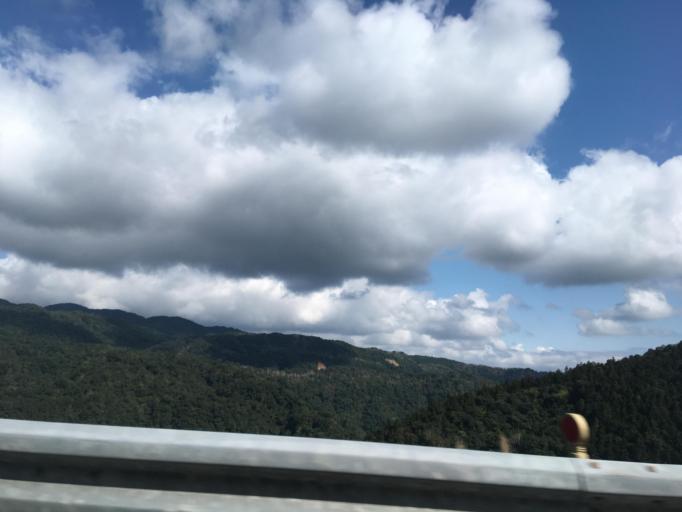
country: TW
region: Taiwan
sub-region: Yilan
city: Yilan
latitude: 24.7479
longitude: 121.6476
